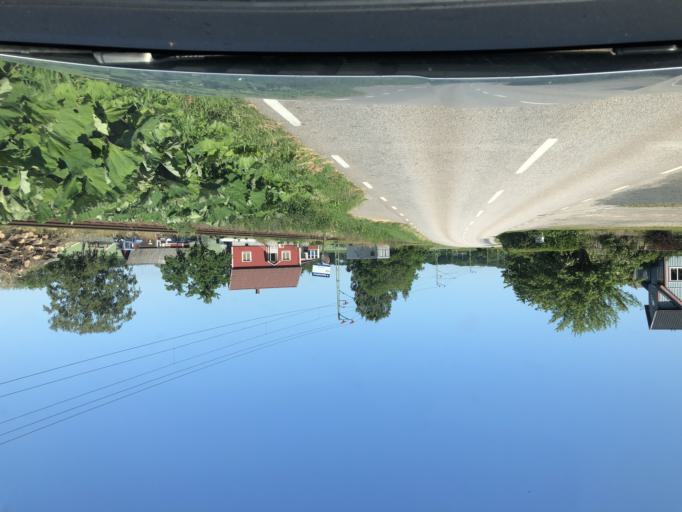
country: SE
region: Blekinge
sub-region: Solvesborgs Kommun
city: Soelvesborg
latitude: 56.1101
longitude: 14.6205
